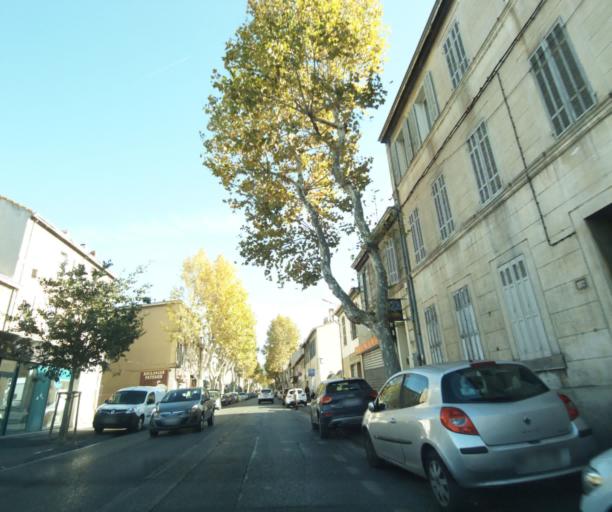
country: FR
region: Provence-Alpes-Cote d'Azur
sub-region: Departement des Bouches-du-Rhone
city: Marseille 11
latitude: 43.2885
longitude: 5.4625
